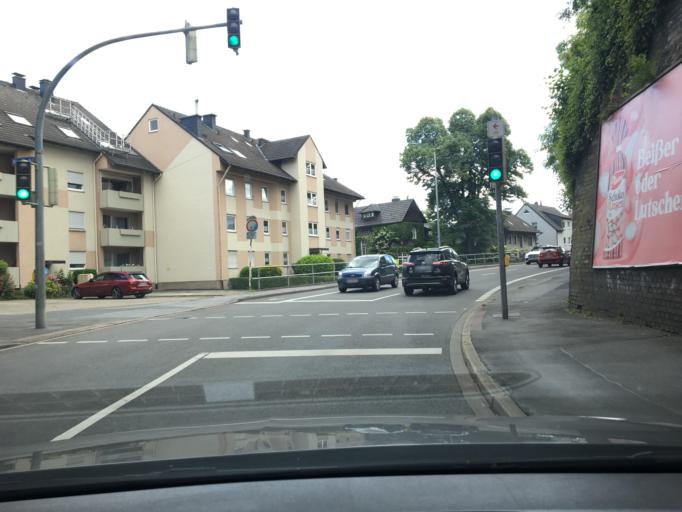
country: DE
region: North Rhine-Westphalia
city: Witten
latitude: 51.5157
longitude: 7.3759
